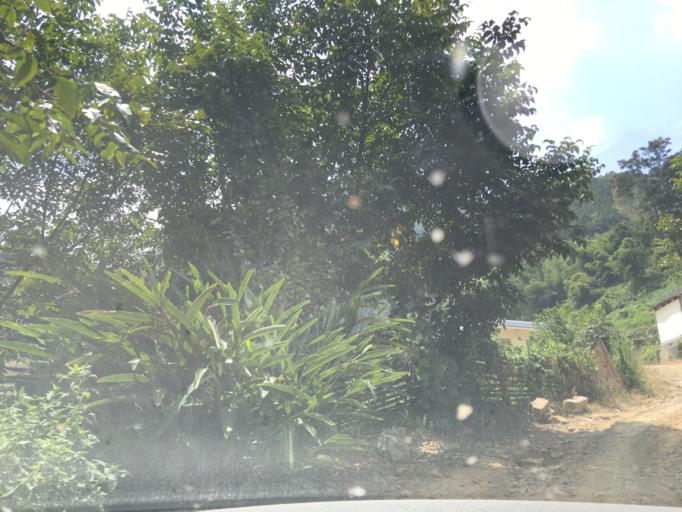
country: CN
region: Guangxi Zhuangzu Zizhiqu
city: Xinzhou
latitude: 24.9546
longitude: 105.7846
